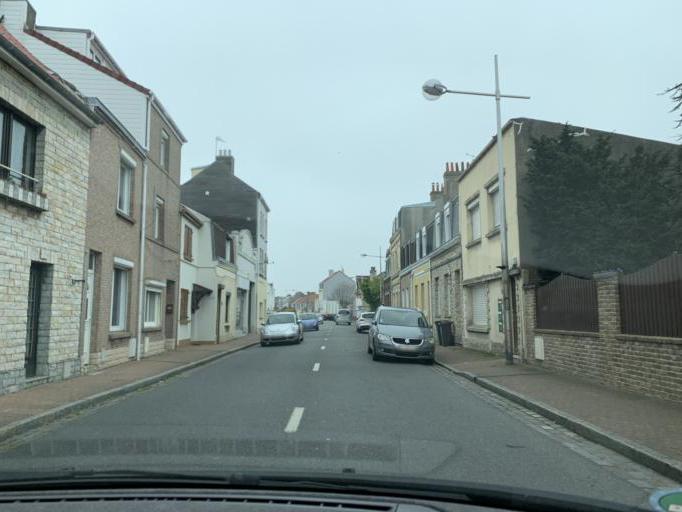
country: FR
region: Nord-Pas-de-Calais
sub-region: Departement du Pas-de-Calais
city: Coquelles
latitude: 50.9573
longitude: 1.8189
